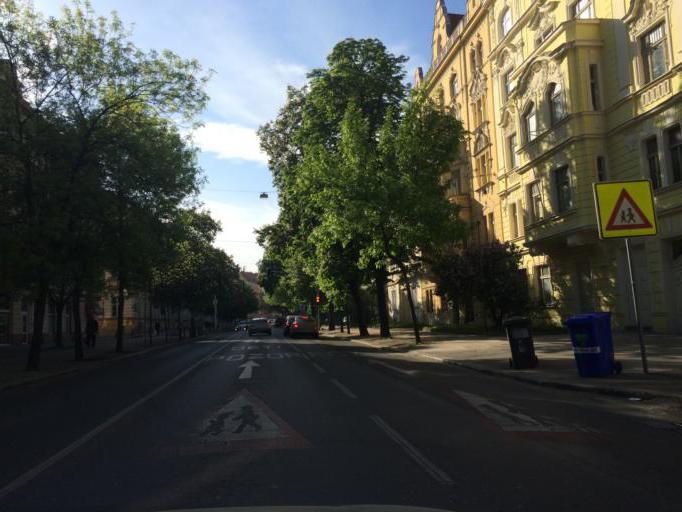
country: CZ
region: Praha
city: Prague
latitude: 50.1012
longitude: 14.4185
